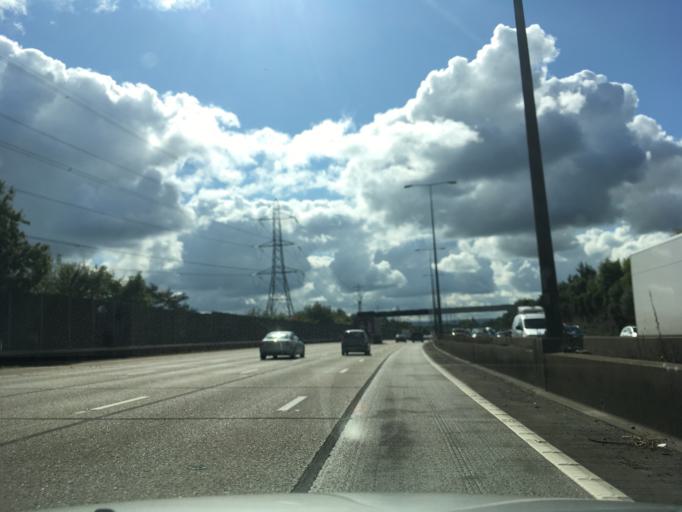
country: GB
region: England
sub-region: Surrey
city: Byfleet
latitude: 51.3469
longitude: -0.4854
